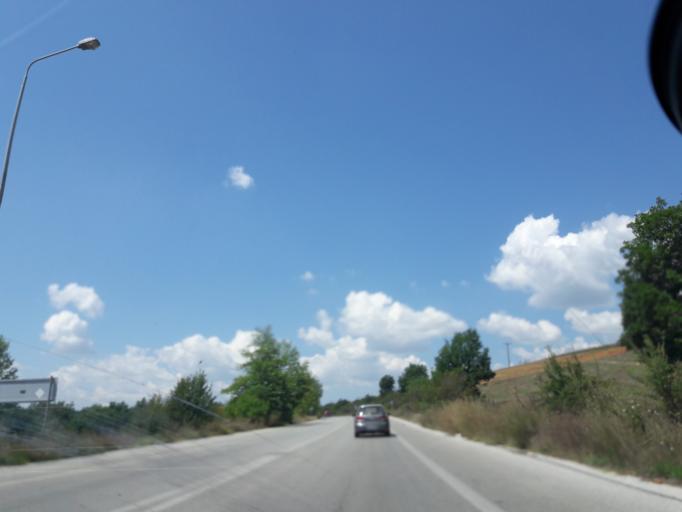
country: GR
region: Central Macedonia
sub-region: Nomos Chalkidikis
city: Galatista
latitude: 40.4652
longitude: 23.3668
